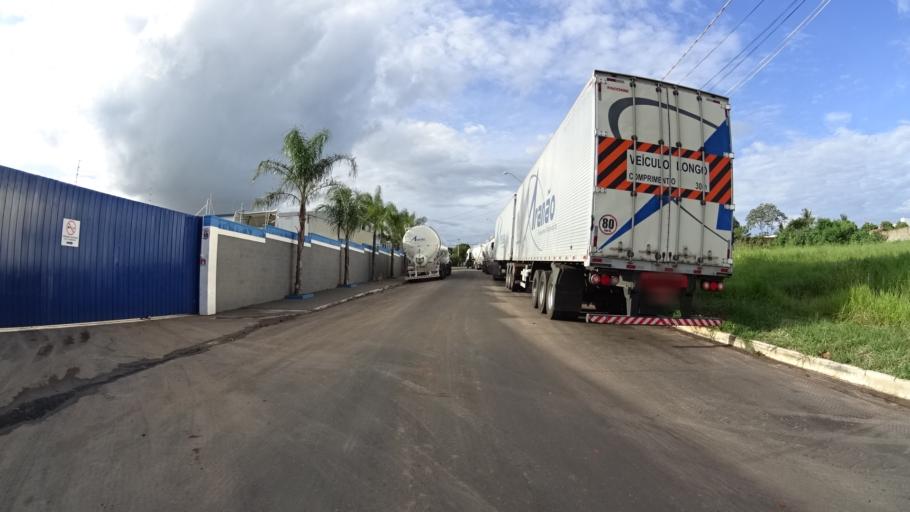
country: BR
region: Sao Paulo
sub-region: Marilia
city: Marilia
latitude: -22.2217
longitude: -49.8844
